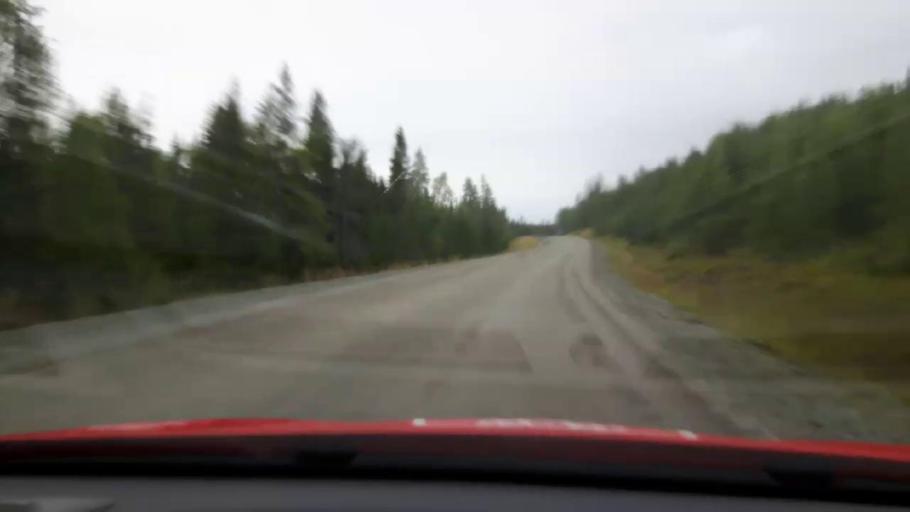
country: SE
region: Jaemtland
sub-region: Are Kommun
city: Are
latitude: 63.4373
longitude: 12.7219
